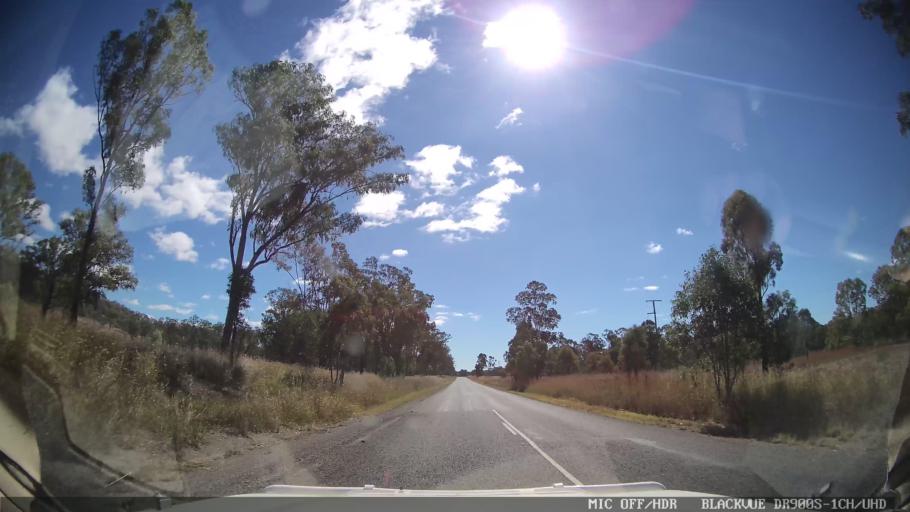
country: AU
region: Queensland
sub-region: Gladstone
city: Toolooa
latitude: -24.4439
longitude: 151.3419
